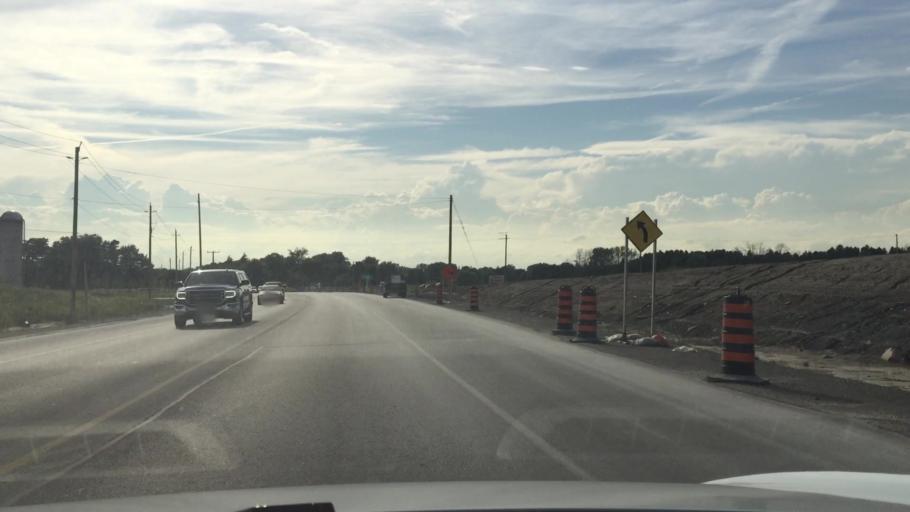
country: CA
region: Ontario
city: Oshawa
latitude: 43.9139
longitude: -78.7687
